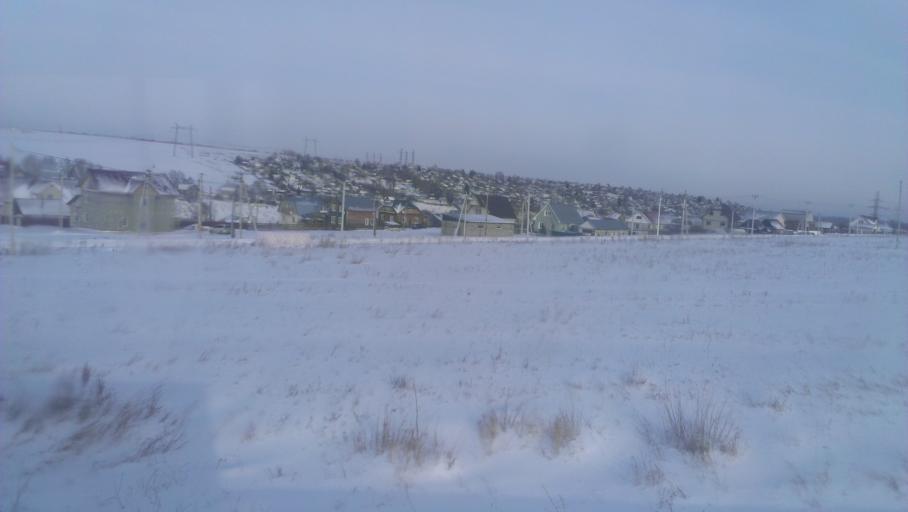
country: RU
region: Altai Krai
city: Gon'ba
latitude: 53.4133
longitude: 83.5544
